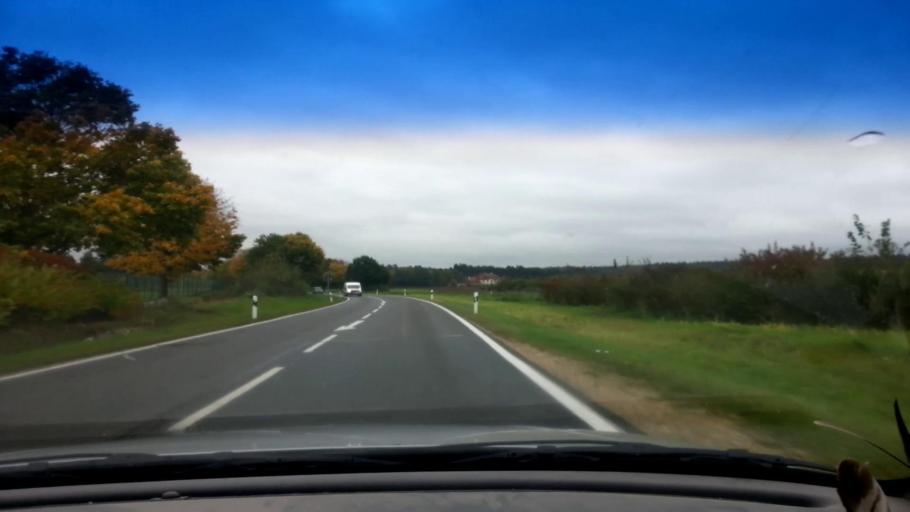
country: DE
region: Bavaria
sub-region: Upper Franconia
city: Memmelsdorf
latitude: 49.9288
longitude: 10.9523
